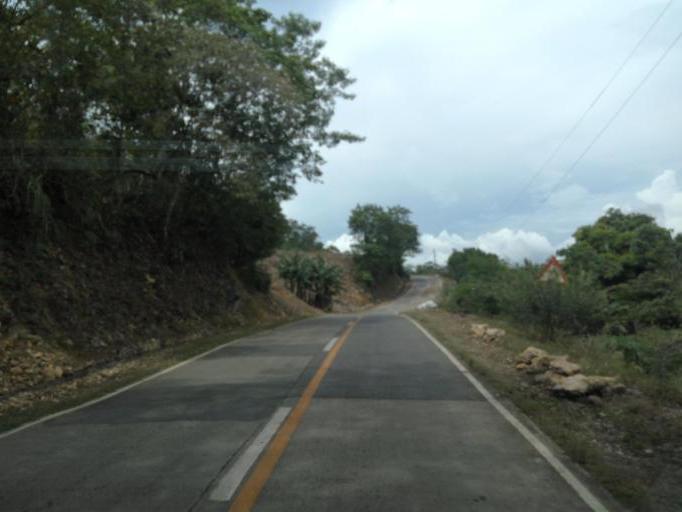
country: PH
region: Cagayan Valley
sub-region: Province of Quirino
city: Dumabato
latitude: 16.2622
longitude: 121.6816
